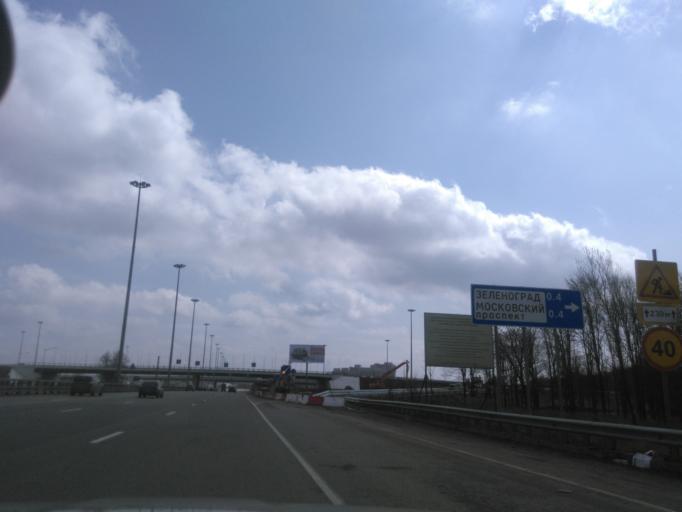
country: RU
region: Moskovskaya
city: Rzhavki
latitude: 56.0015
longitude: 37.2397
